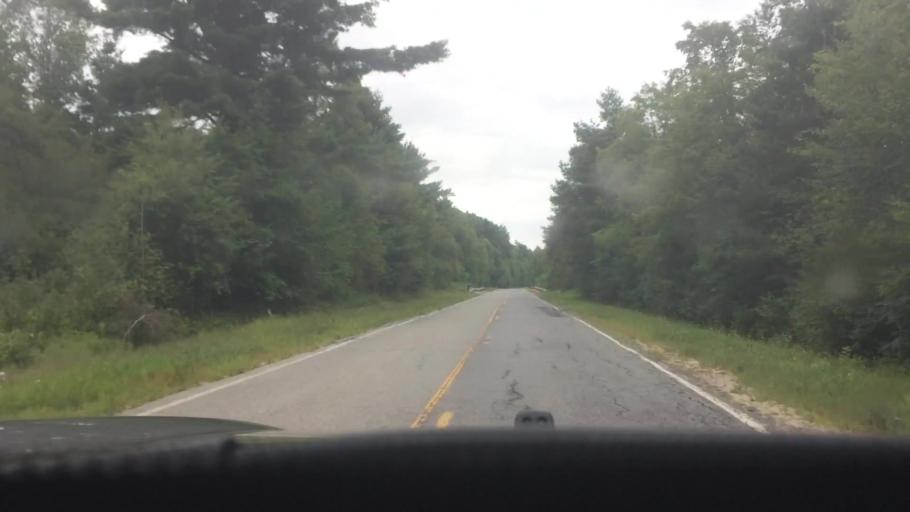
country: US
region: New York
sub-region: St. Lawrence County
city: Hannawa Falls
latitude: 44.5661
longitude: -74.9175
